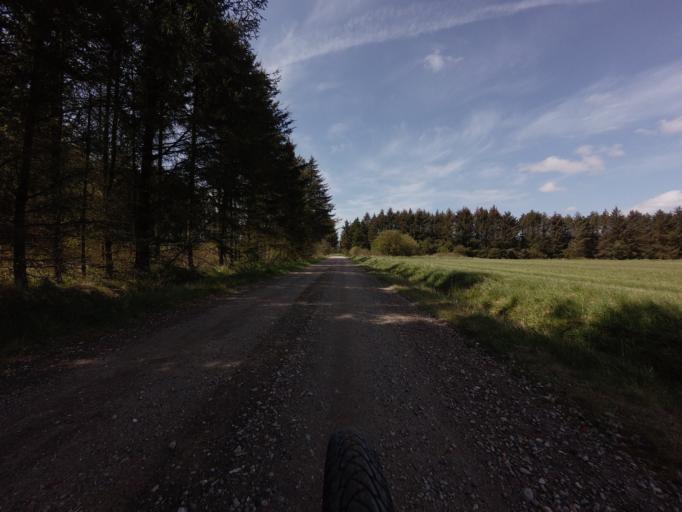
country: DK
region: North Denmark
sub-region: Jammerbugt Kommune
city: Brovst
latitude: 57.1564
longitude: 9.5593
